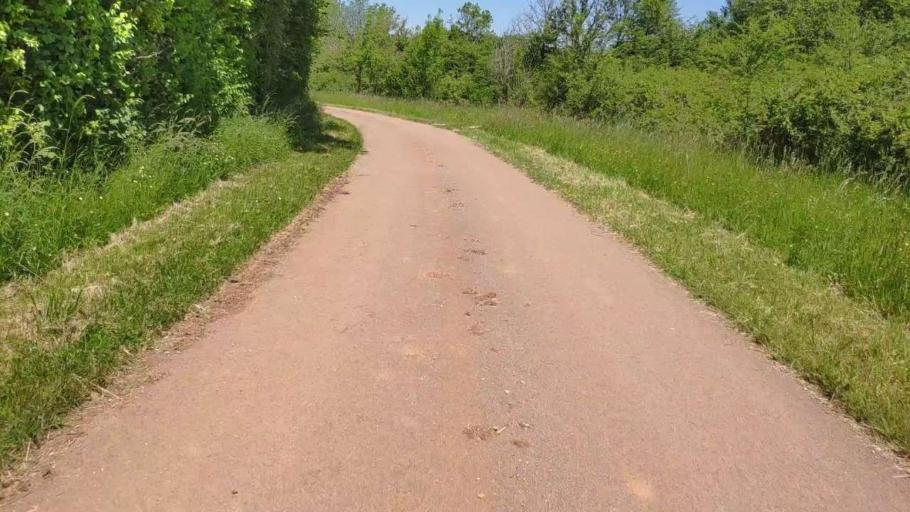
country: FR
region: Franche-Comte
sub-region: Departement du Jura
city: Perrigny
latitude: 46.7227
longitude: 5.6455
